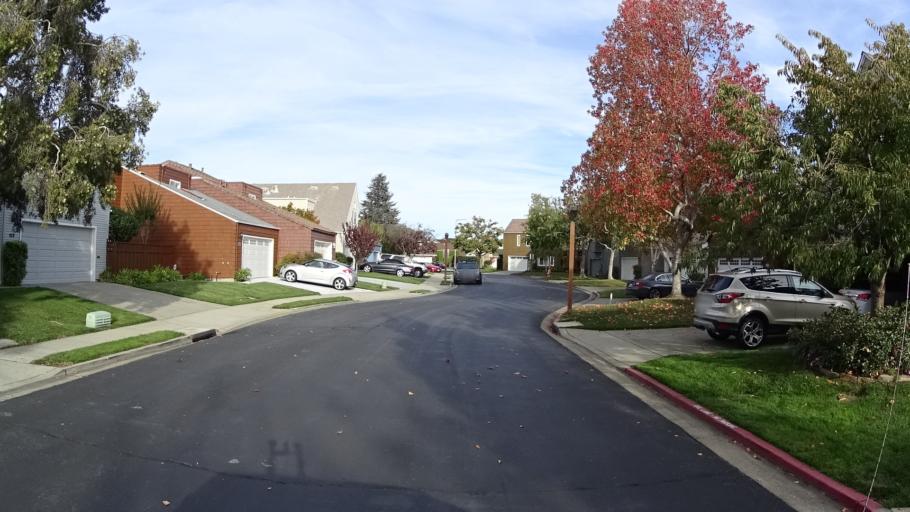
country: US
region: California
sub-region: San Mateo County
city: Foster City
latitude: 37.5445
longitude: -122.2681
